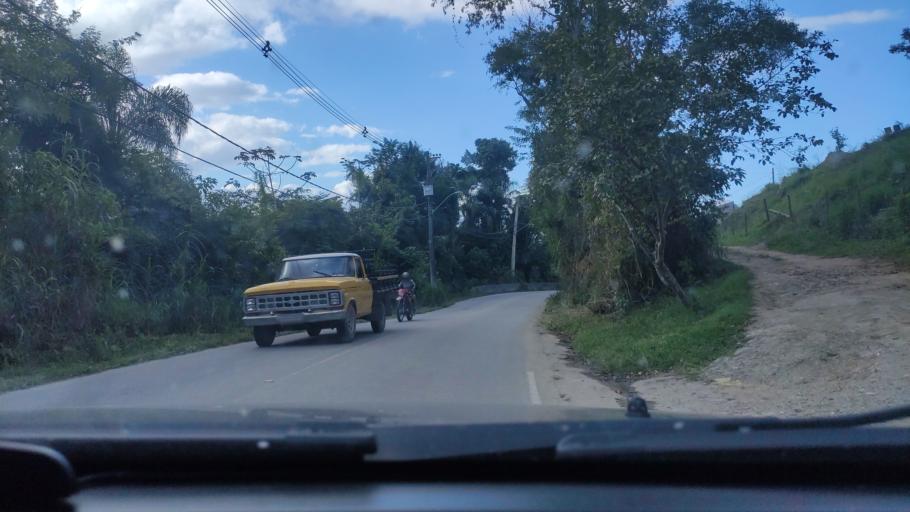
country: BR
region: Sao Paulo
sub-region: Sao Sebastiao
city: Sao Sebastiao
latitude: -23.6989
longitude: -45.4829
